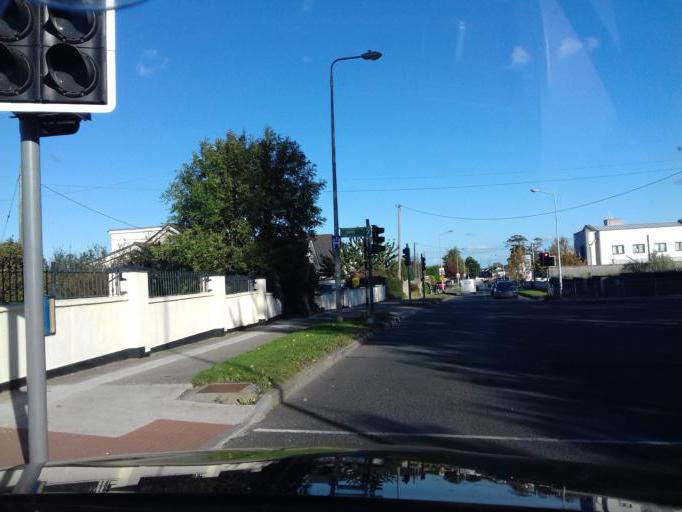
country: IE
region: Leinster
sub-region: Lu
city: Drogheda
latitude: 53.7148
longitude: -6.3761
